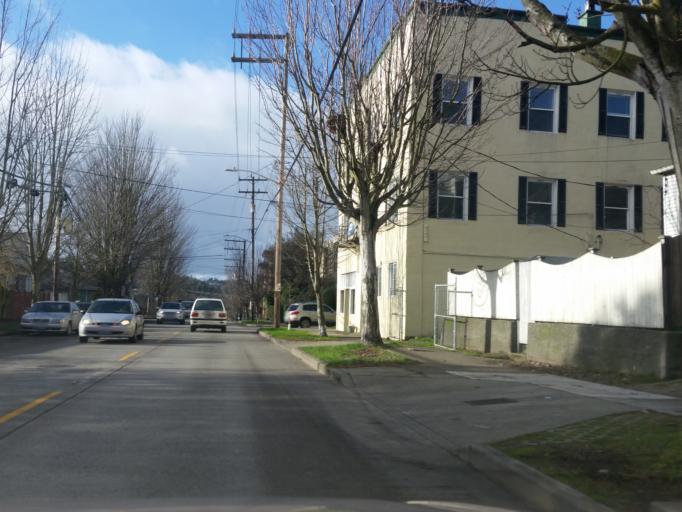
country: US
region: Washington
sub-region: King County
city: Seattle
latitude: 47.6542
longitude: -122.3565
